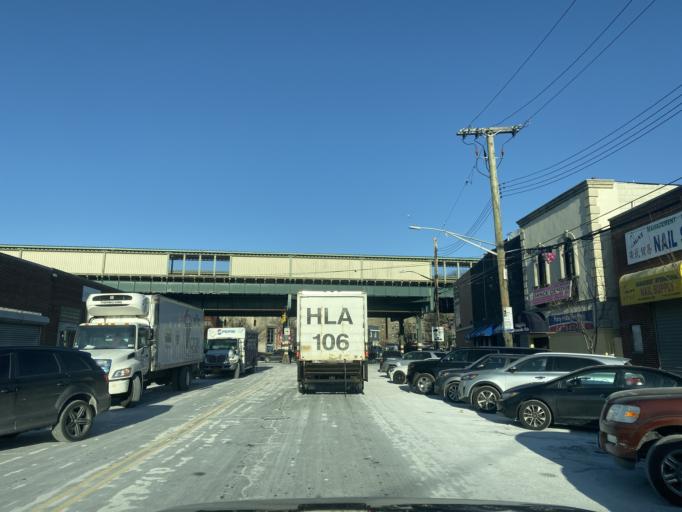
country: US
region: New York
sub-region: Bronx
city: The Bronx
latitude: 40.8394
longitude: -73.8426
